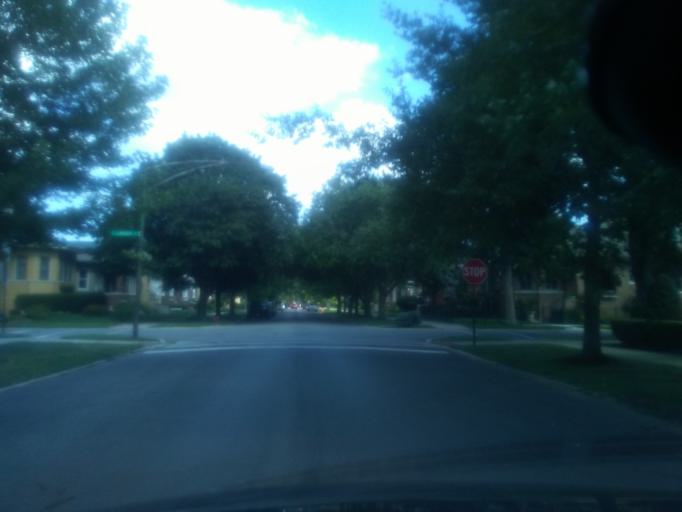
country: US
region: Illinois
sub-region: Cook County
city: Harwood Heights
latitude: 41.9587
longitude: -87.7651
